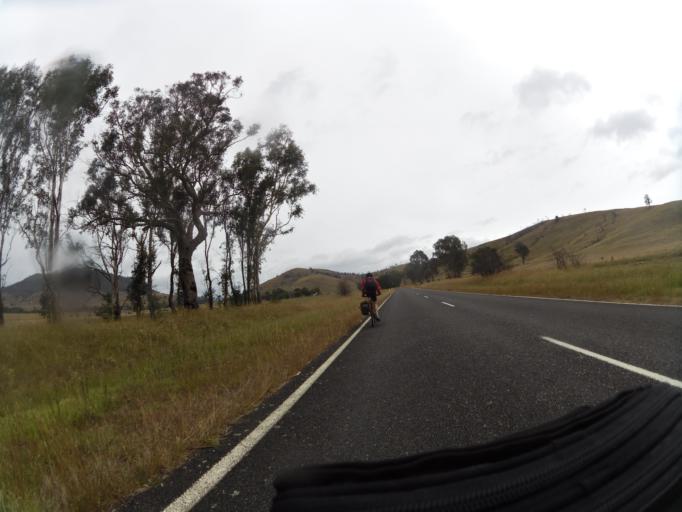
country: AU
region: New South Wales
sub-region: Greater Hume Shire
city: Holbrook
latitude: -36.2073
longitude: 147.7375
